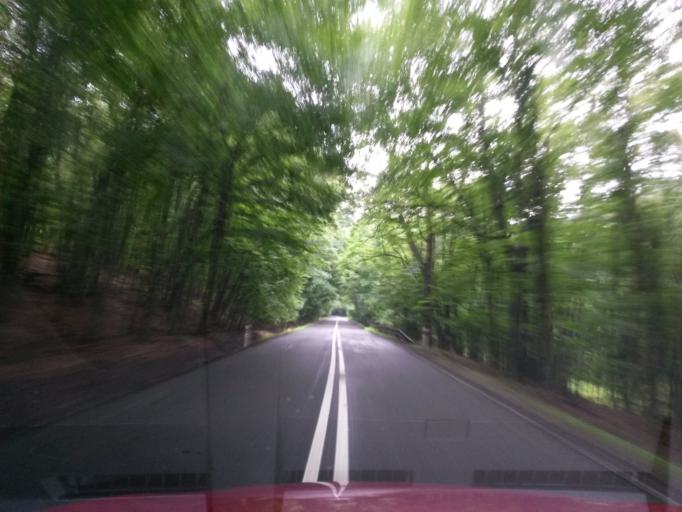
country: SK
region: Nitriansky
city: Sahy
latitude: 48.1766
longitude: 19.0325
